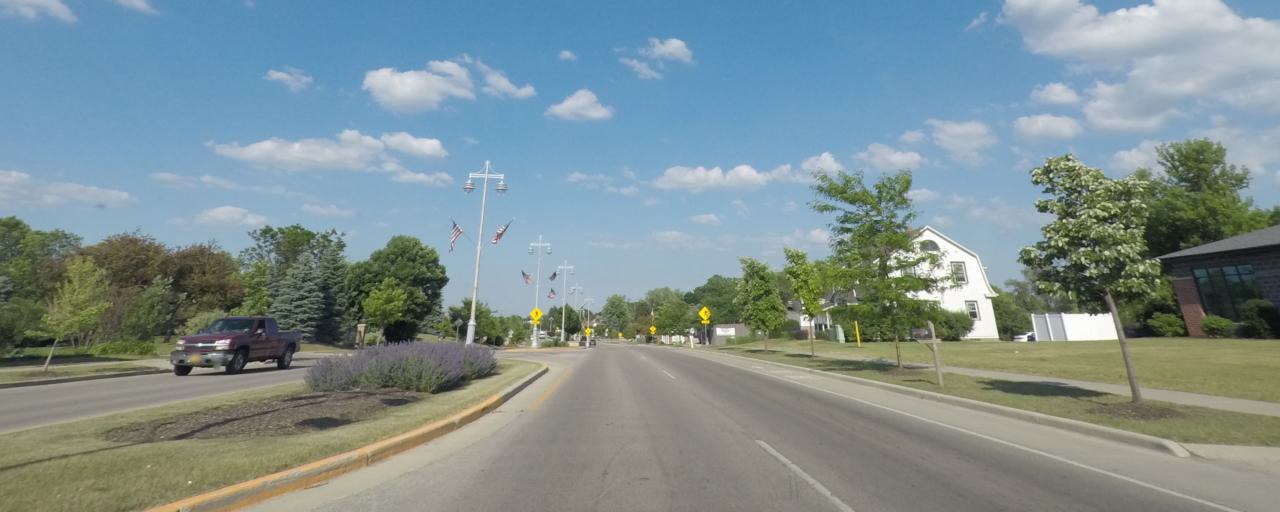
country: US
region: Wisconsin
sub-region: Waukesha County
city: Muskego
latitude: 42.9063
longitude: -88.1374
